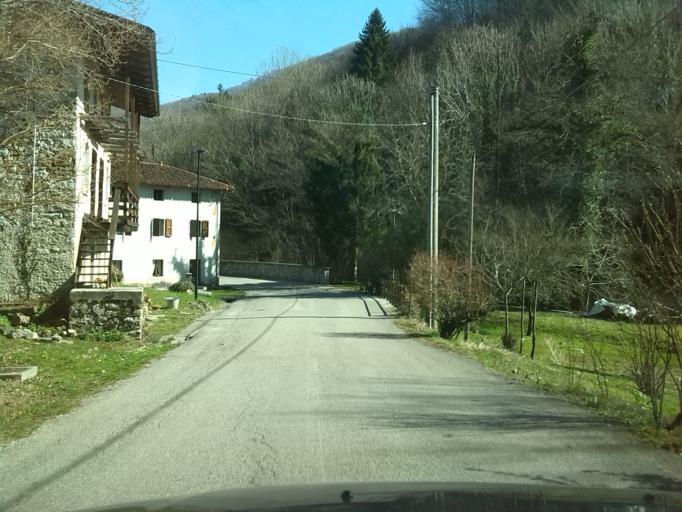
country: IT
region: Friuli Venezia Giulia
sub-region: Provincia di Udine
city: Savogna
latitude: 46.1598
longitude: 13.5341
